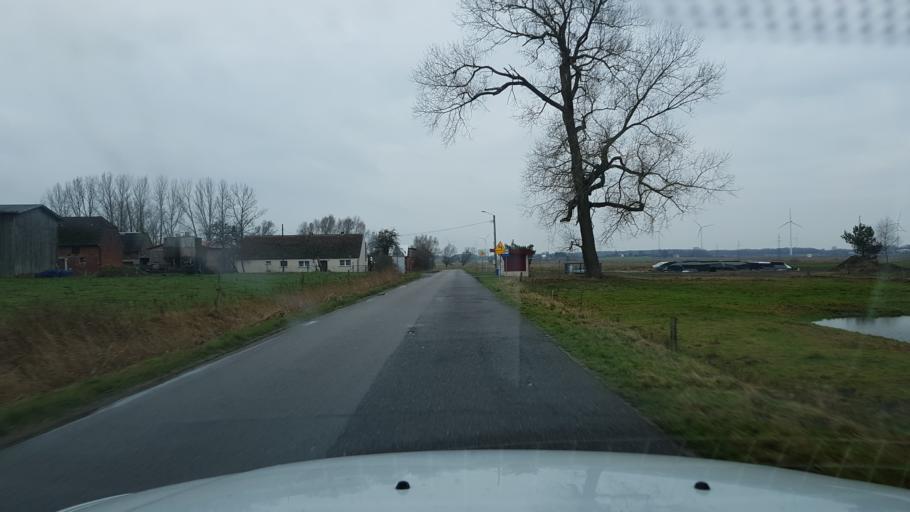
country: PL
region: West Pomeranian Voivodeship
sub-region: Powiat kolobrzeski
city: Grzybowo
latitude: 54.1311
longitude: 15.4702
